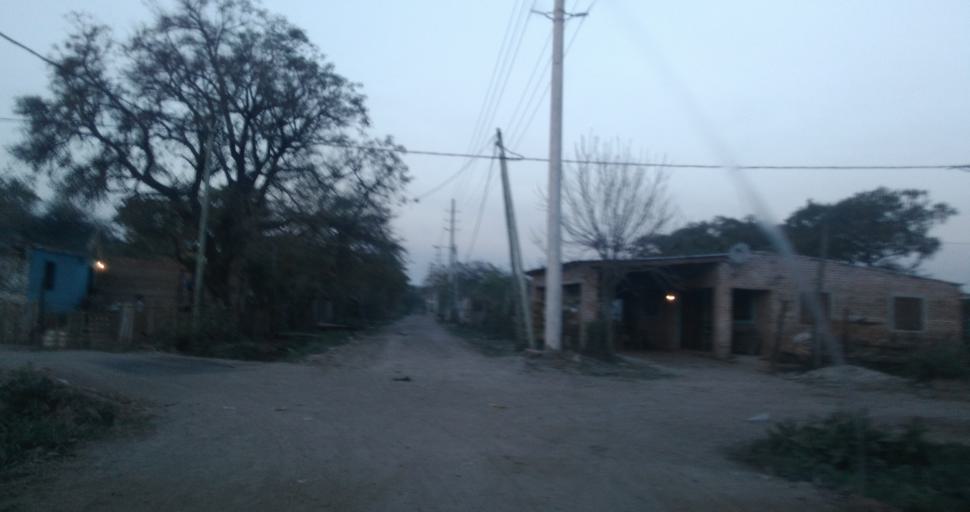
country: AR
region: Chaco
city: Fontana
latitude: -27.4254
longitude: -58.9898
